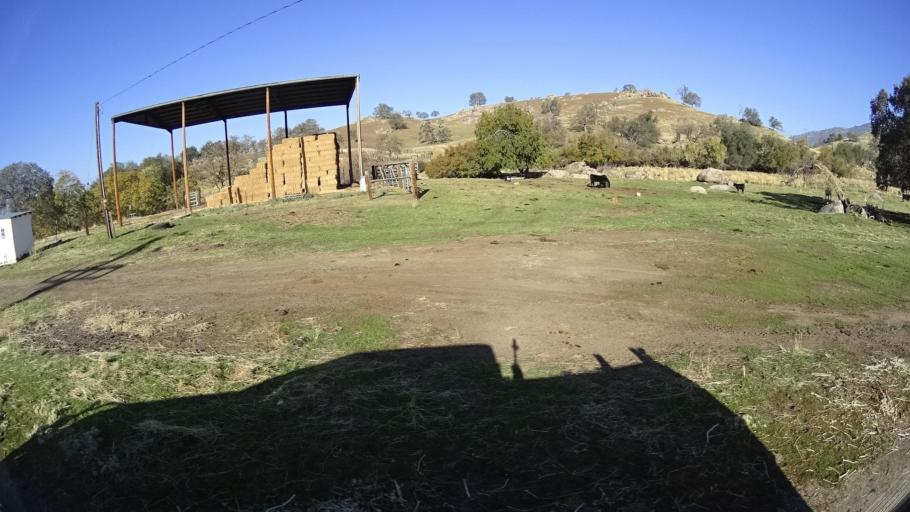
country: US
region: California
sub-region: Kern County
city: Alta Sierra
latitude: 35.7221
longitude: -118.8100
